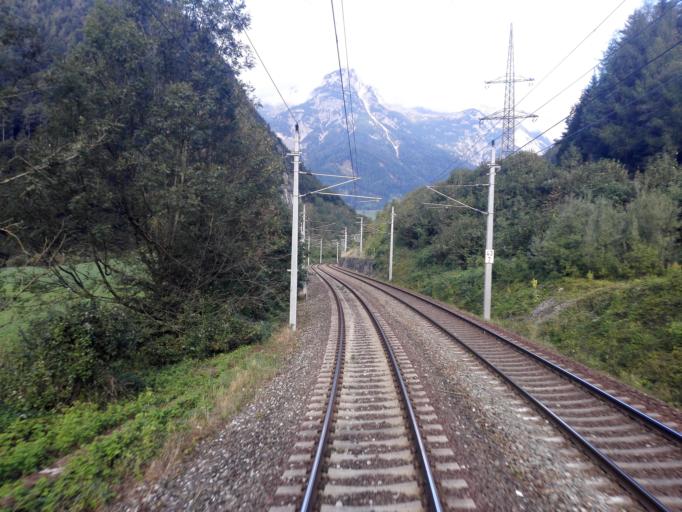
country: AT
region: Salzburg
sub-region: Politischer Bezirk Sankt Johann im Pongau
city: Werfen
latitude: 47.4847
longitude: 13.1894
